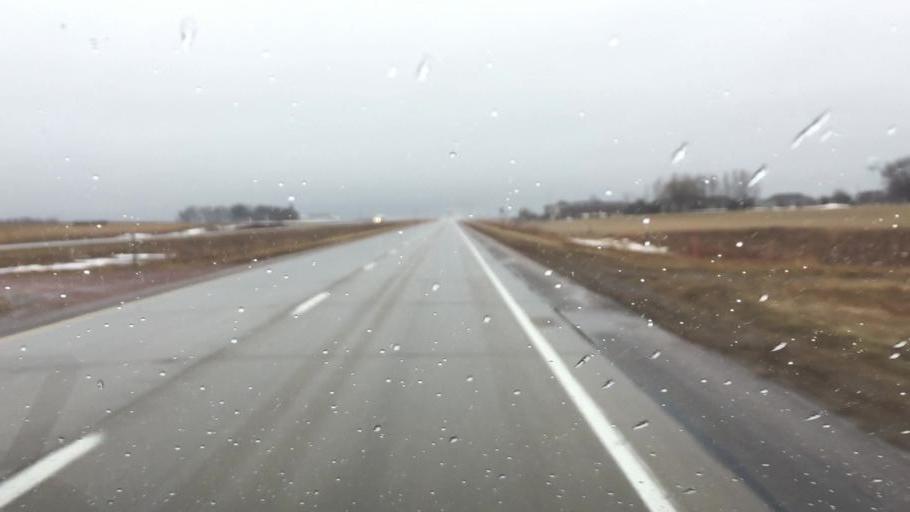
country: US
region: Iowa
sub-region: O'Brien County
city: Sheldon
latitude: 43.0768
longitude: -95.8989
